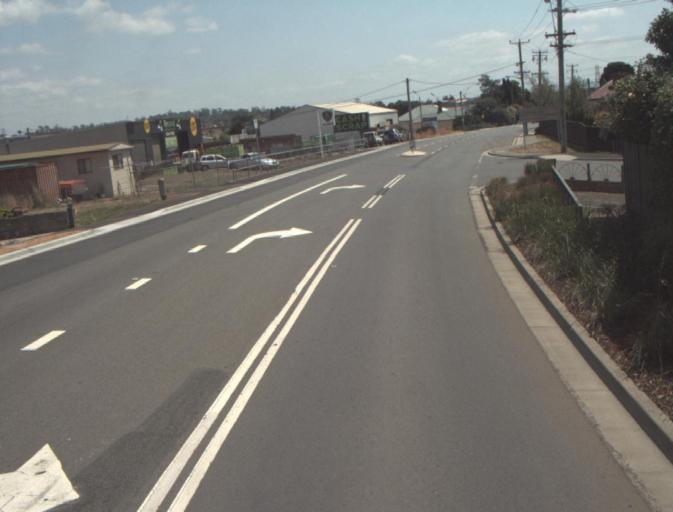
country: AU
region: Tasmania
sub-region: Launceston
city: Summerhill
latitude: -41.4921
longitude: 147.1686
